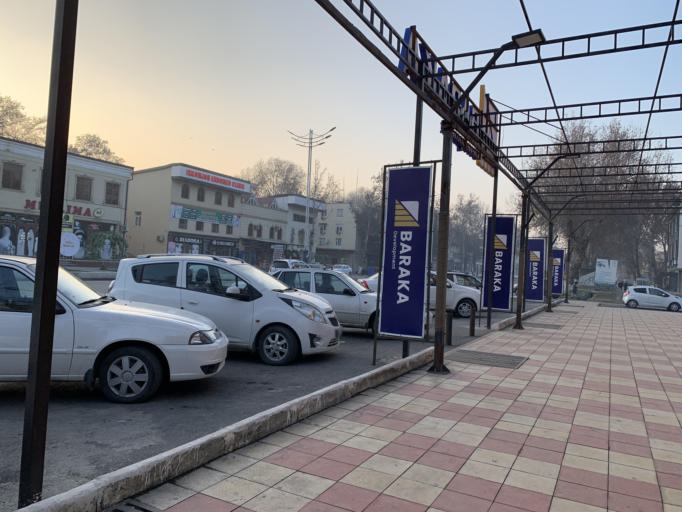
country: UZ
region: Fergana
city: Qo`qon
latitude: 40.5473
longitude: 70.9270
